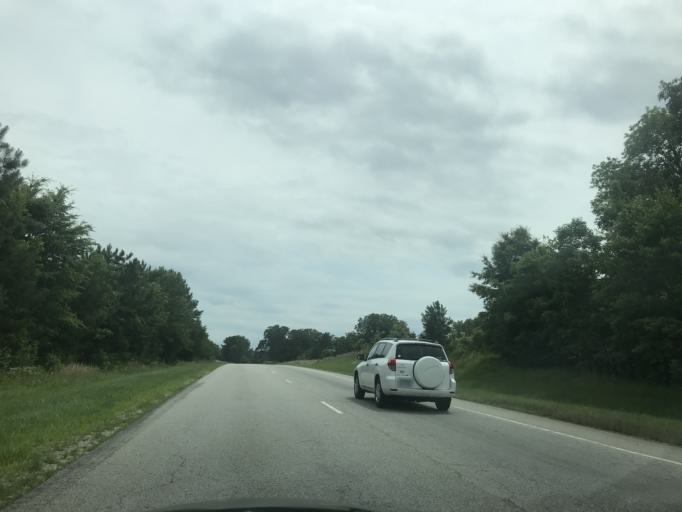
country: US
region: North Carolina
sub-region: Franklin County
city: Franklinton
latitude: 36.1639
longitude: -78.4521
